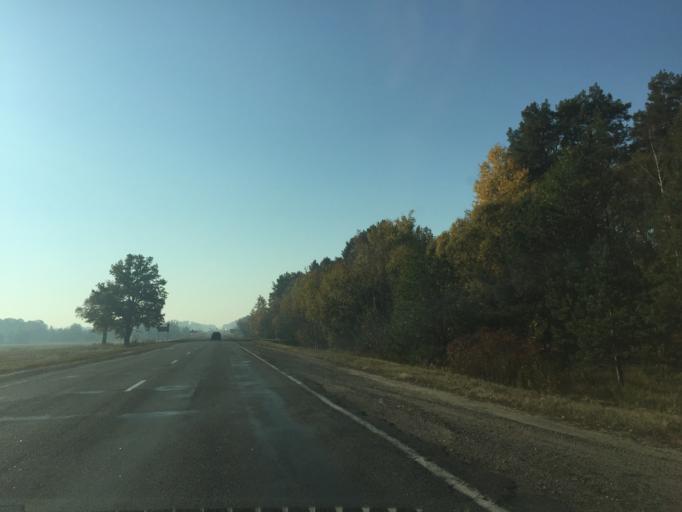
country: BY
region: Gomel
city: Gomel
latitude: 52.3971
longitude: 30.8287
